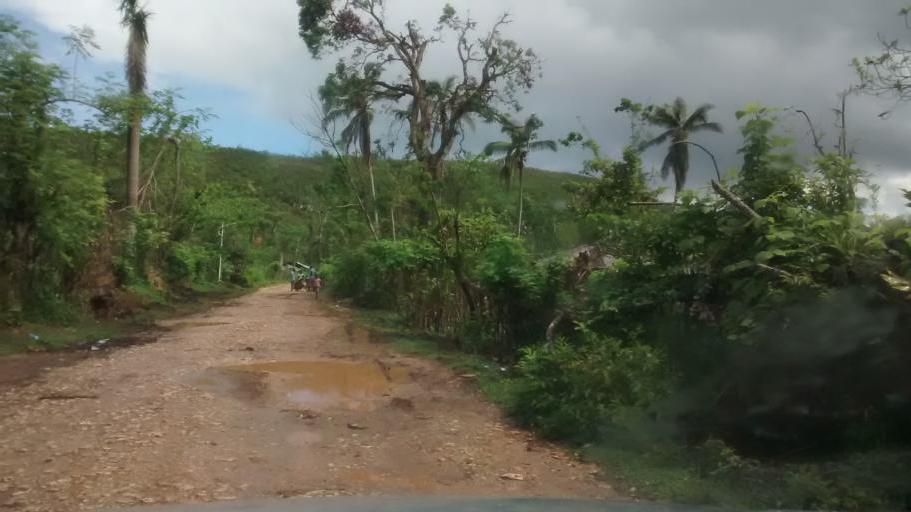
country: HT
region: Grandans
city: Corail
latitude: 18.5367
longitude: -73.9364
